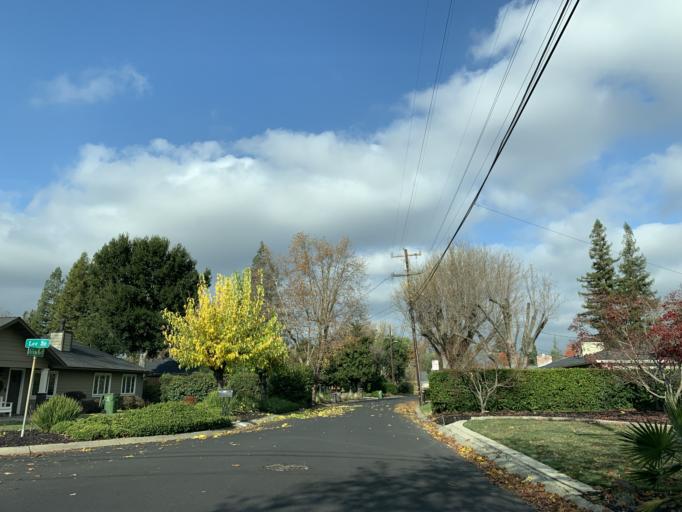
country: US
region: California
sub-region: Contra Costa County
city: Saranap
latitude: 37.8884
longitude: -122.0615
